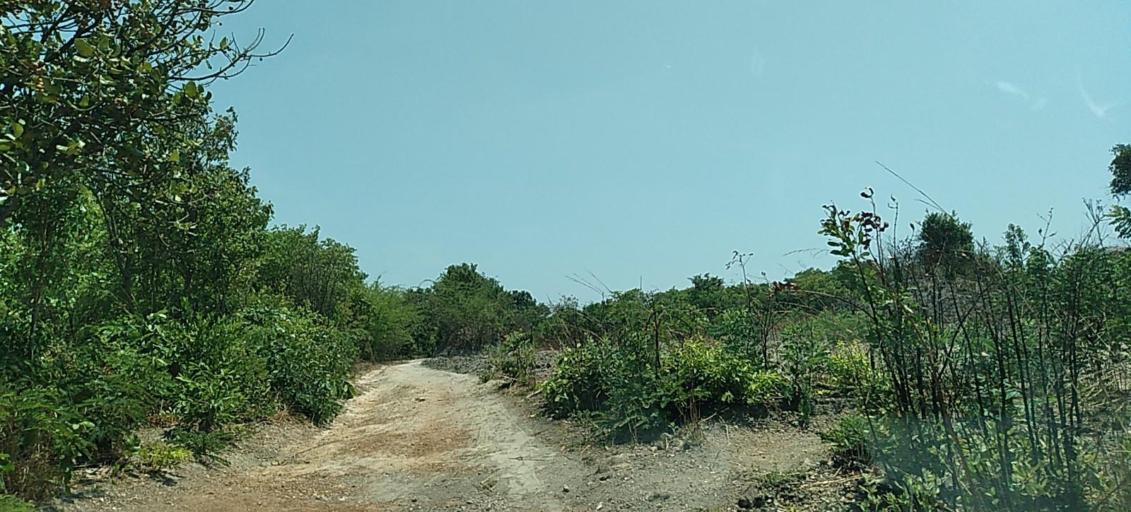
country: ZM
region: Copperbelt
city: Luanshya
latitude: -12.9848
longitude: 28.3291
